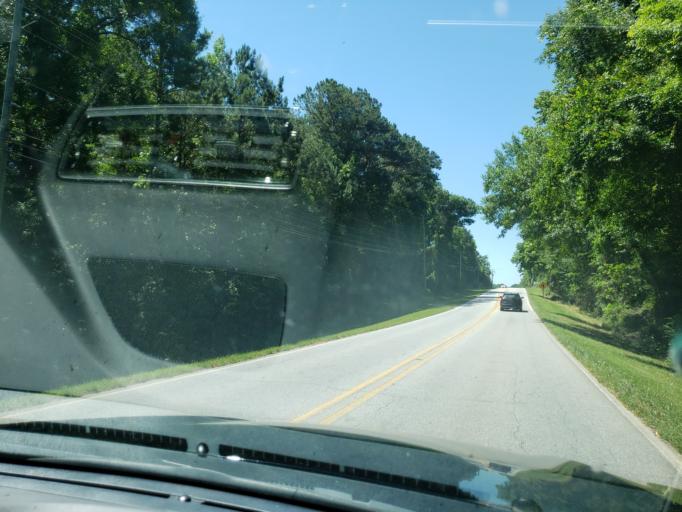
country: US
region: Alabama
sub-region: Lee County
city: Auburn
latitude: 32.6426
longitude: -85.4814
